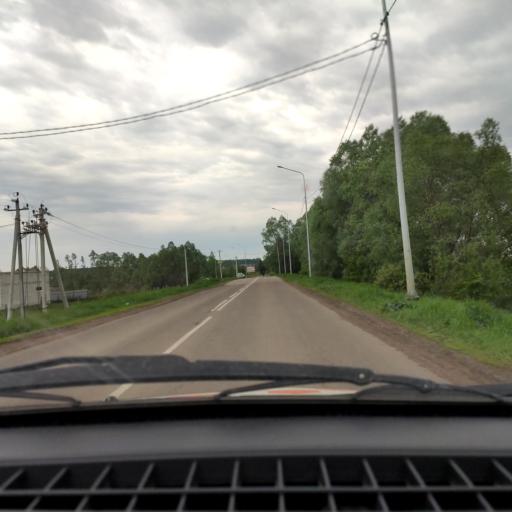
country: RU
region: Bashkortostan
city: Avdon
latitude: 54.5527
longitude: 55.7576
